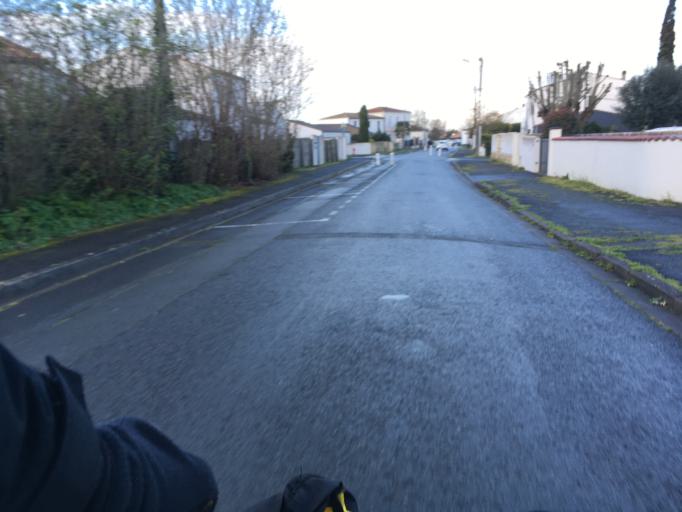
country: FR
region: Poitou-Charentes
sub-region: Departement de la Charente-Maritime
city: Nieul-sur-Mer
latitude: 46.2061
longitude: -1.1676
